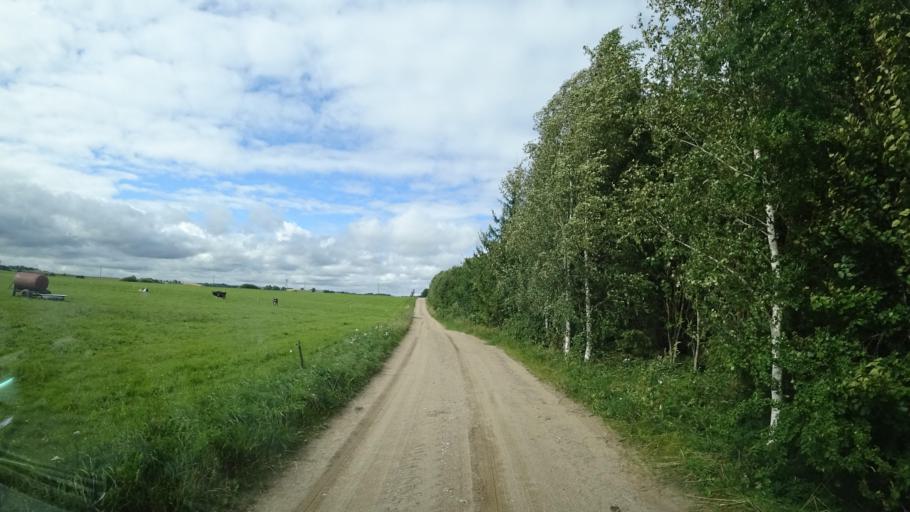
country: PL
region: Podlasie
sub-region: Suwalki
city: Suwalki
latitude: 54.3740
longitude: 22.9021
